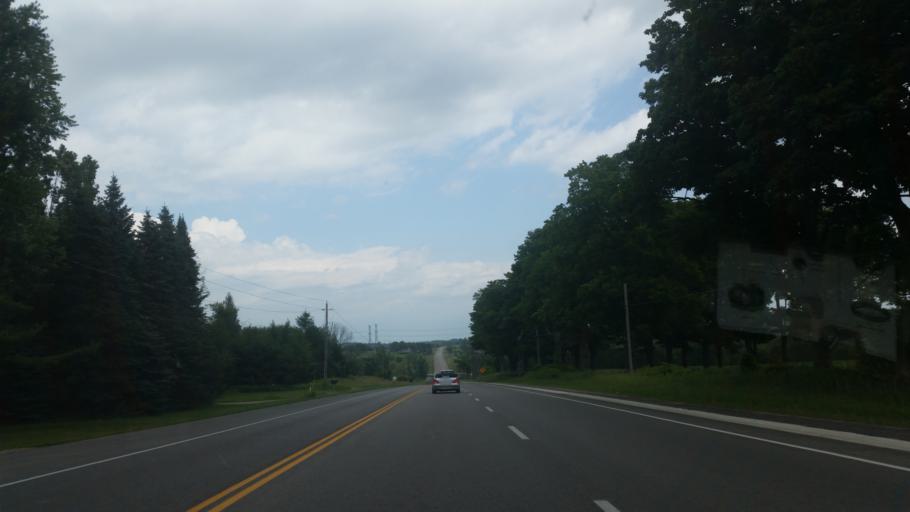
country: CA
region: Ontario
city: Orangeville
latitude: 43.7134
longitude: -80.1172
